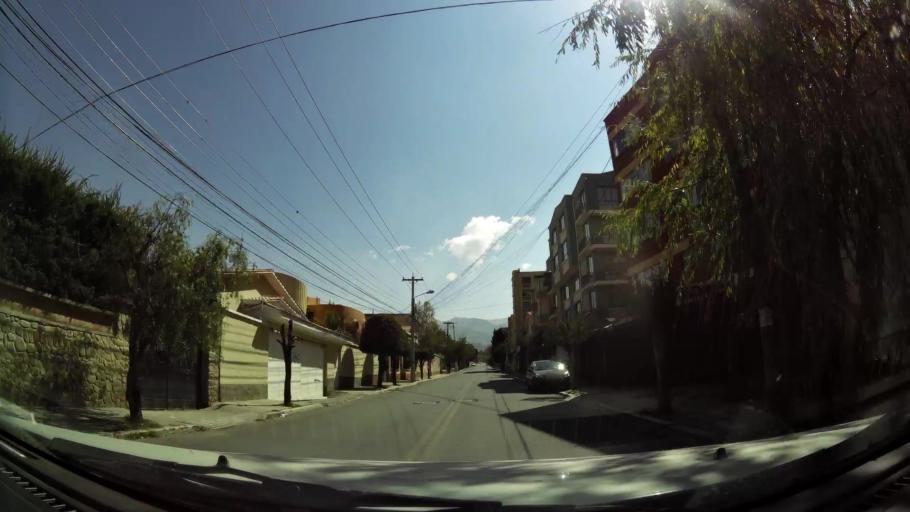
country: BO
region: La Paz
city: La Paz
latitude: -16.5161
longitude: -68.0862
